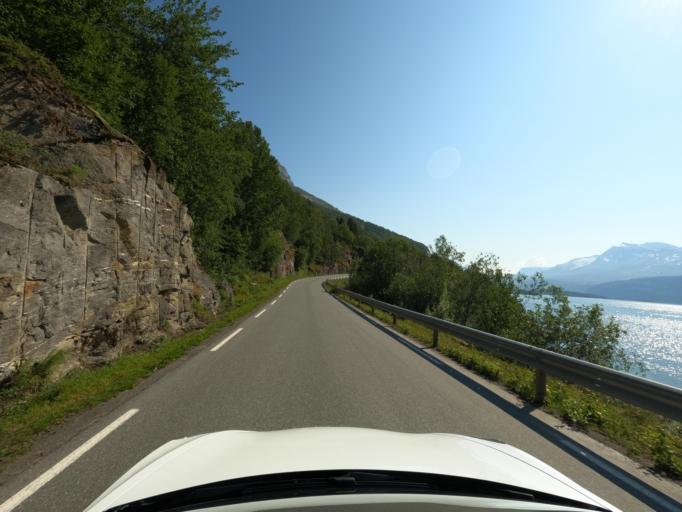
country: NO
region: Nordland
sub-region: Narvik
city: Narvik
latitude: 68.3568
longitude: 17.2710
